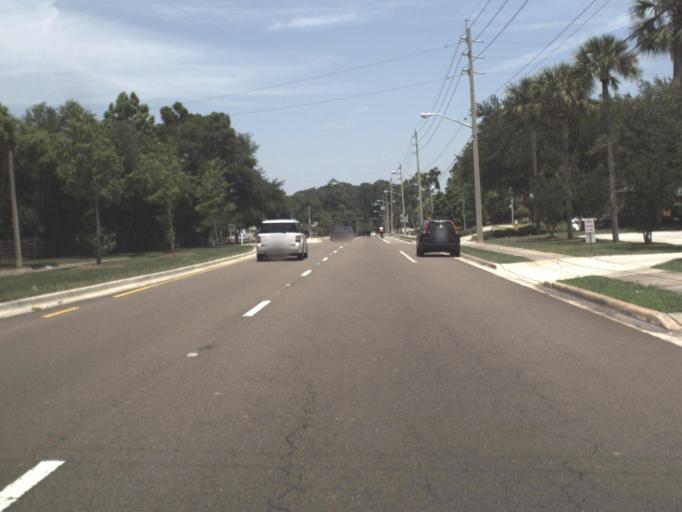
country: US
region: Florida
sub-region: Duval County
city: Jacksonville
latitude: 30.2789
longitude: -81.6506
